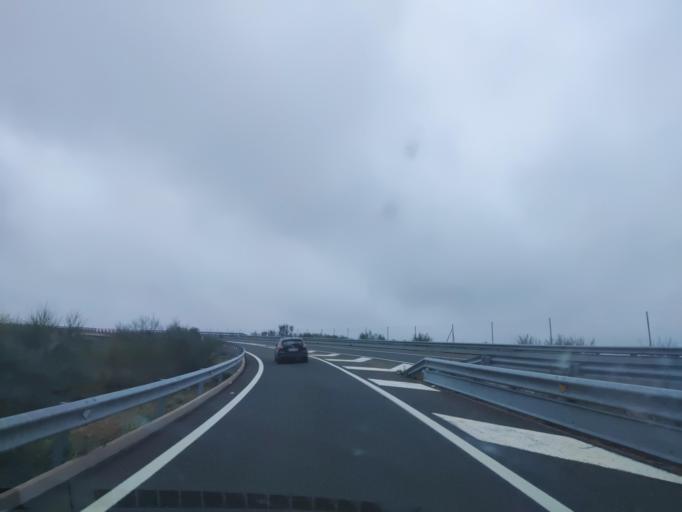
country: ES
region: Castille-La Mancha
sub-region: Province of Toledo
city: Bargas
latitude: 39.9387
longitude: -4.0450
